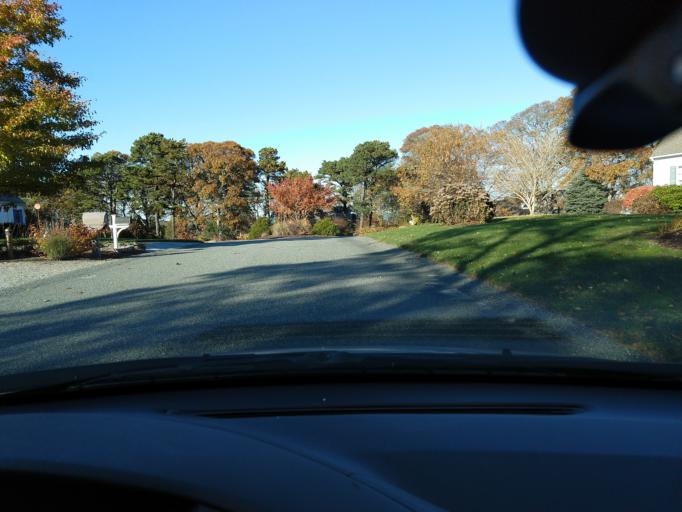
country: US
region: Massachusetts
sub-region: Barnstable County
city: Orleans
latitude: 41.7808
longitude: -70.0297
